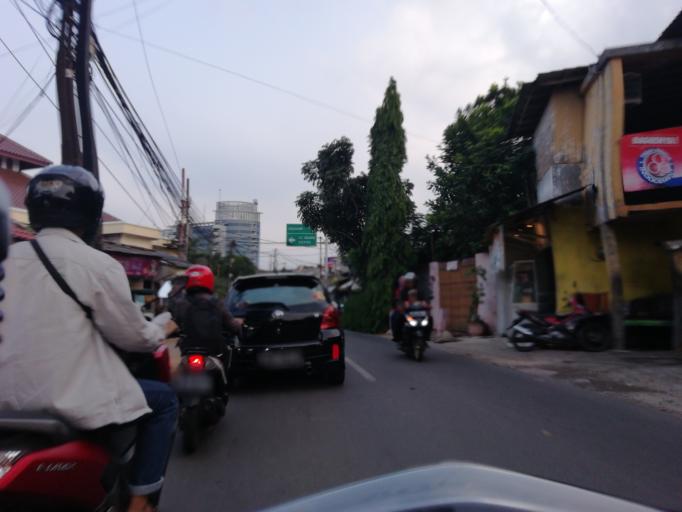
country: ID
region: West Java
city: Depok
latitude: -6.3447
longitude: 106.8261
